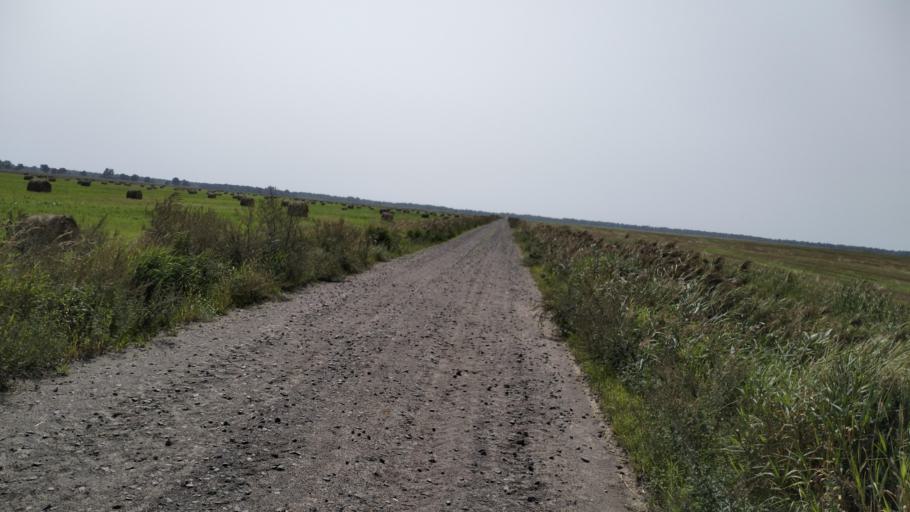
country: BY
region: Brest
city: Davyd-Haradok
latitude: 51.9934
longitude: 27.1762
